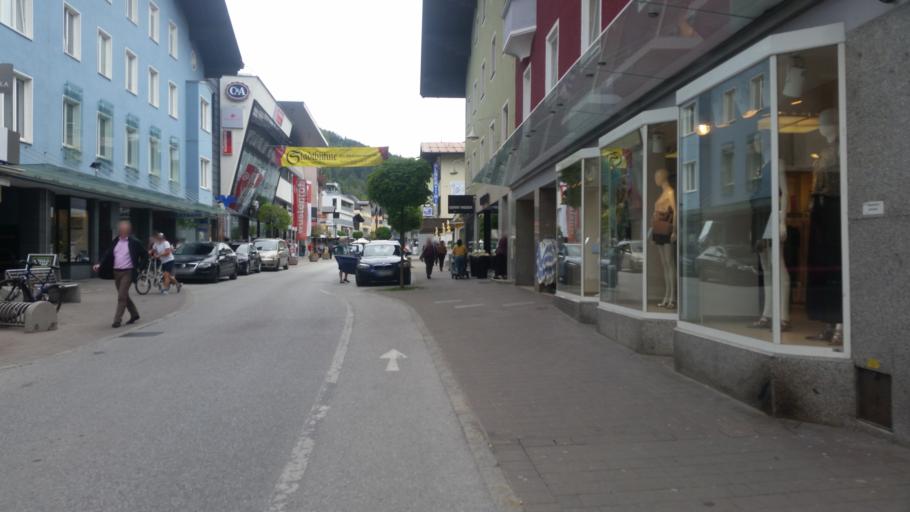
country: AT
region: Tyrol
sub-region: Politischer Bezirk Kufstein
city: Worgl
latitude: 47.4890
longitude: 12.0629
